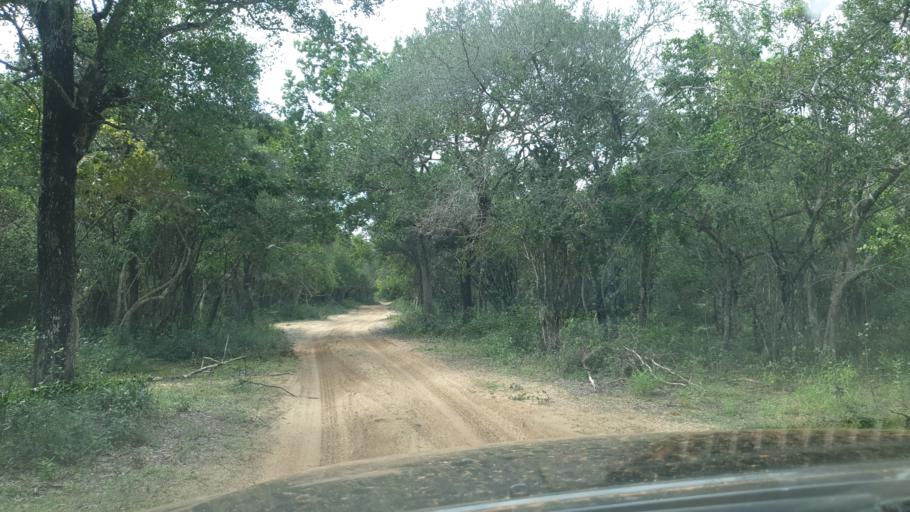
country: LK
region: North Western
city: Puttalam
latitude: 8.4185
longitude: 80.0042
